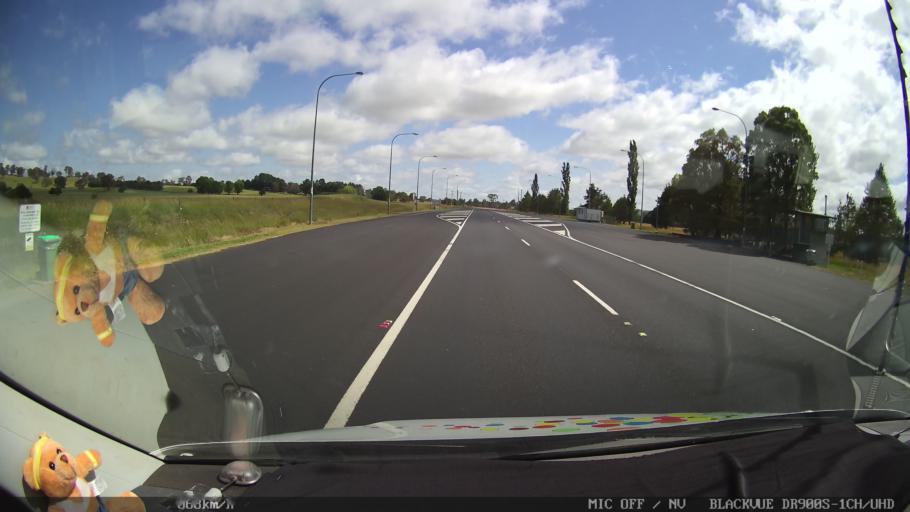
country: AU
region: New South Wales
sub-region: Glen Innes Severn
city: Glen Innes
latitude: -29.9233
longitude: 151.7243
